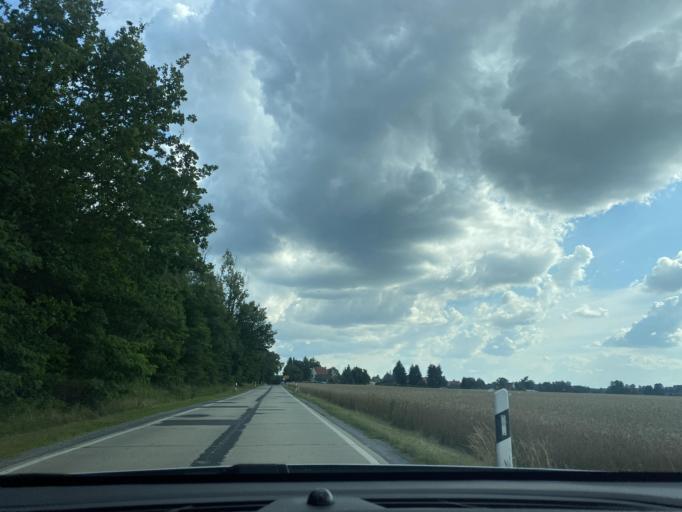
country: DE
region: Saxony
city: Klitten
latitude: 51.3565
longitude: 14.6075
